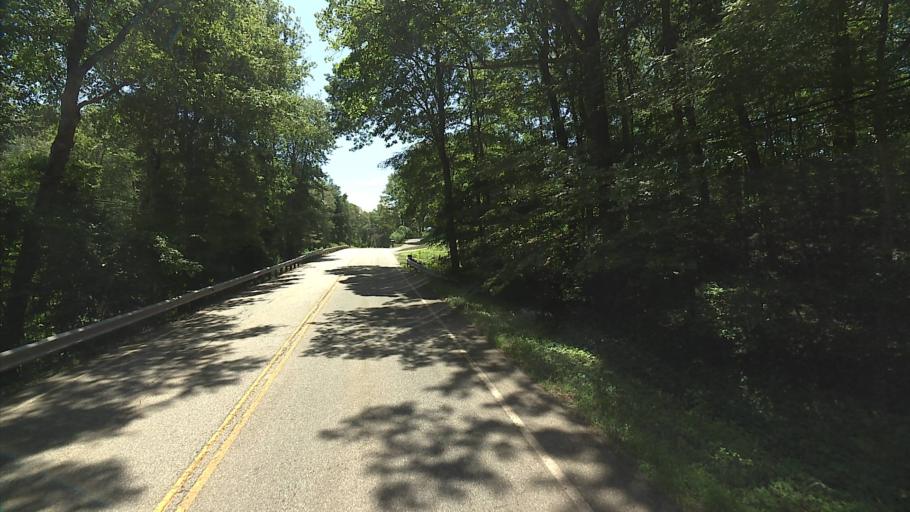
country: US
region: Connecticut
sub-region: Middlesex County
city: East Hampton
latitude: 41.5452
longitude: -72.5052
